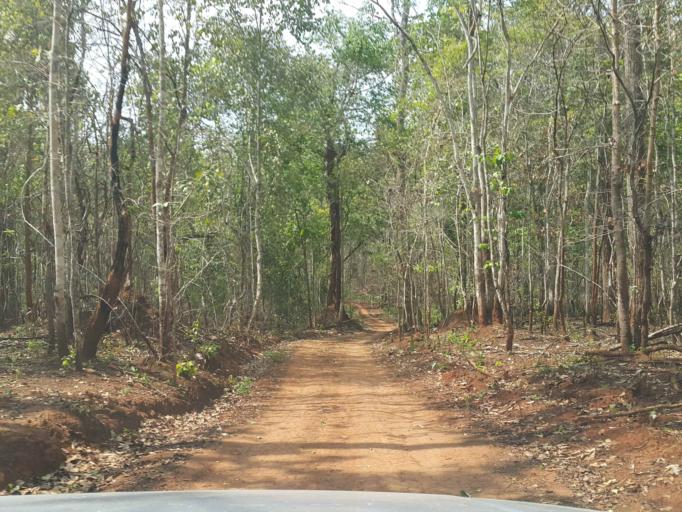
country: TH
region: Chiang Mai
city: Wiang Haeng
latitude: 19.3229
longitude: 98.7210
